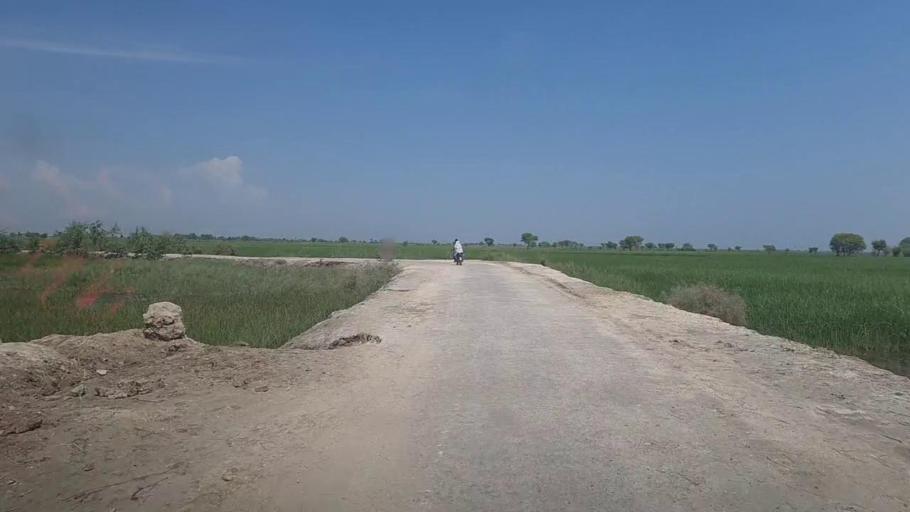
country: PK
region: Sindh
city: Kandhkot
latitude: 28.2888
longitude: 69.2388
